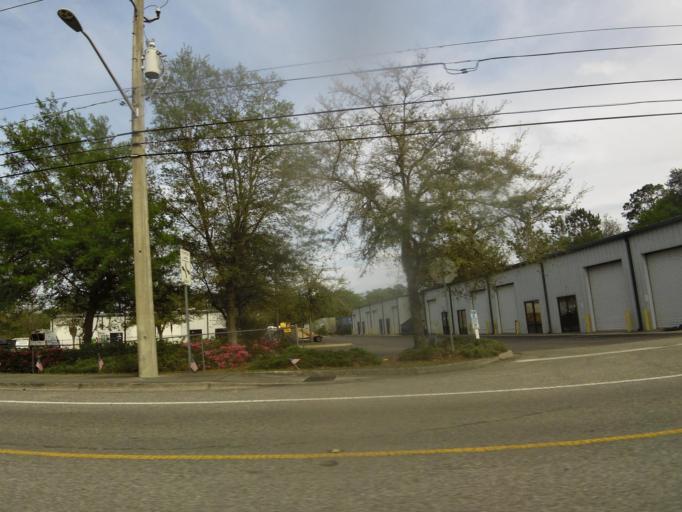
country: US
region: Florida
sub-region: Clay County
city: Bellair-Meadowbrook Terrace
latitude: 30.2711
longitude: -81.7716
